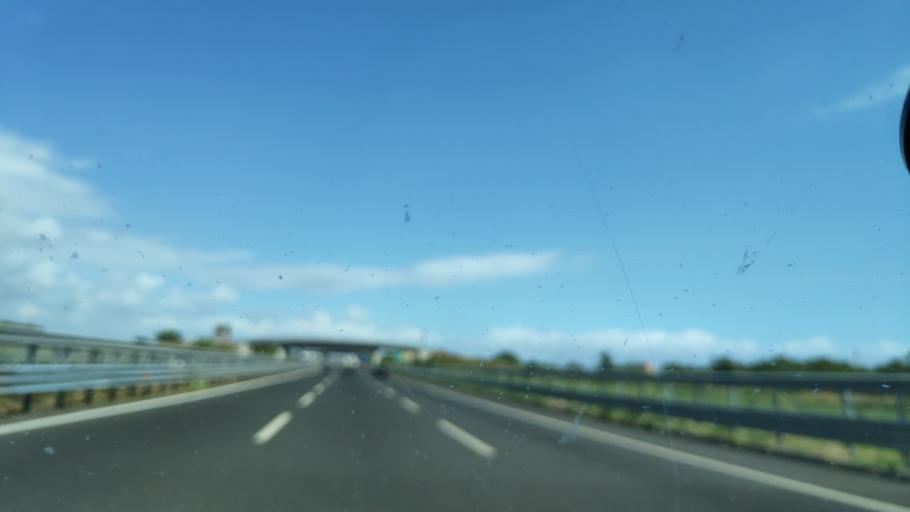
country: IT
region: Campania
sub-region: Provincia di Salerno
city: Pontecagnano
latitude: 40.6513
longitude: 14.8764
